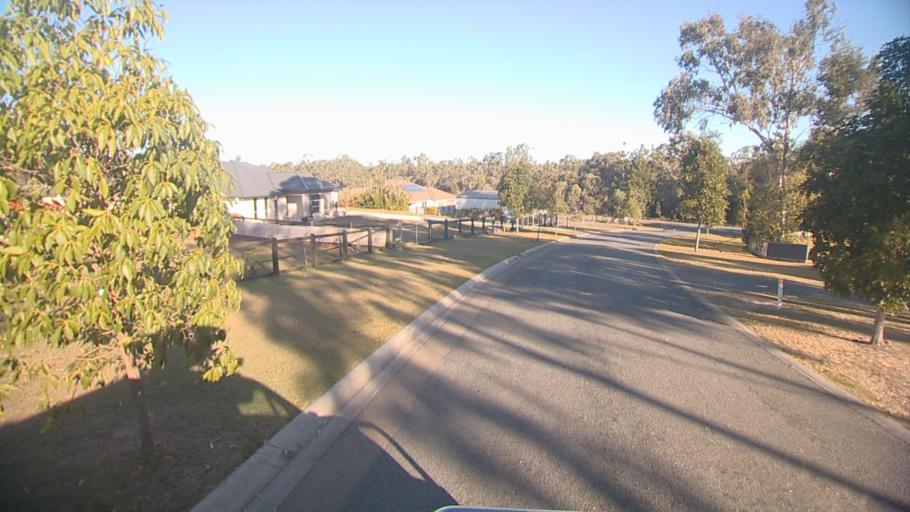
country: AU
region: Queensland
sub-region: Logan
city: North Maclean
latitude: -27.7501
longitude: 152.9663
